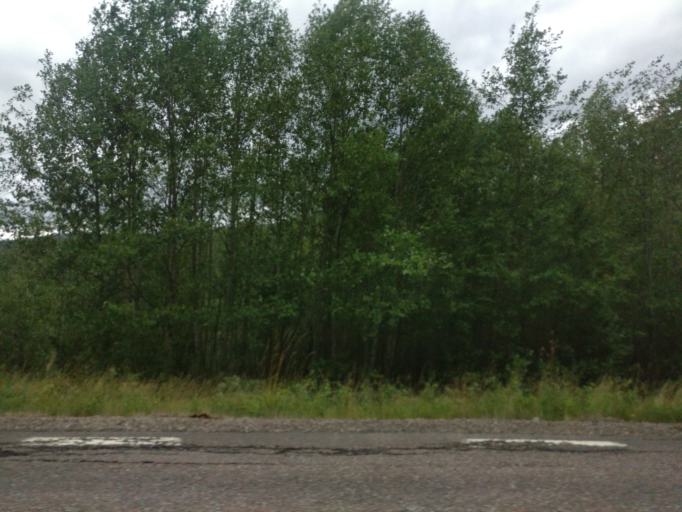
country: SE
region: Vaermland
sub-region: Torsby Kommun
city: Torsby
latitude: 60.5957
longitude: 13.0718
